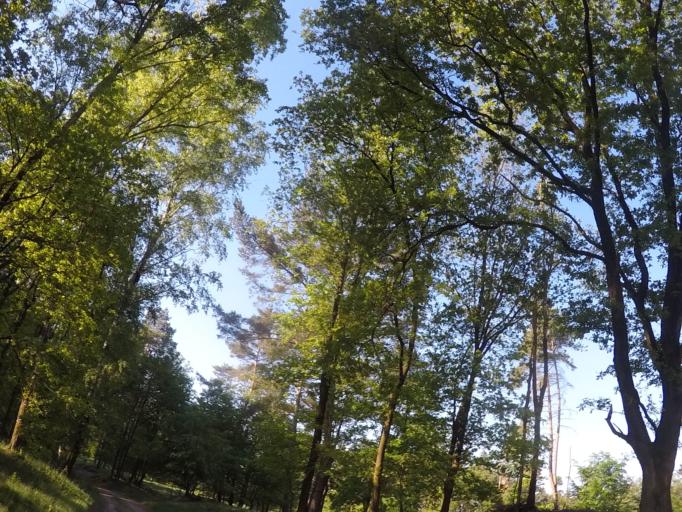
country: NL
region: Gelderland
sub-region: Gemeente Montferland
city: s-Heerenberg
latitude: 51.8848
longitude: 6.1907
